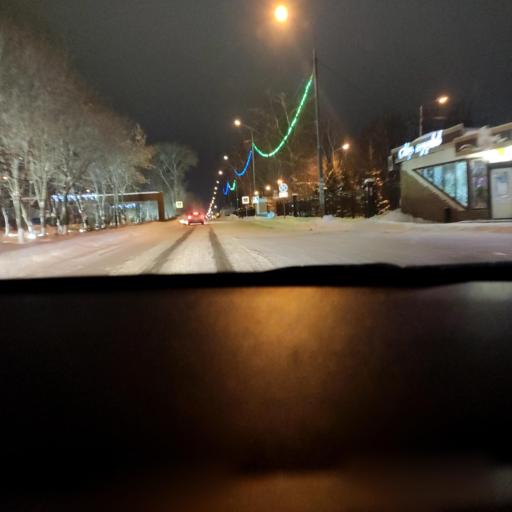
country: RU
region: Tatarstan
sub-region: Chistopol'skiy Rayon
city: Chistopol'
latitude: 55.3638
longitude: 50.6455
